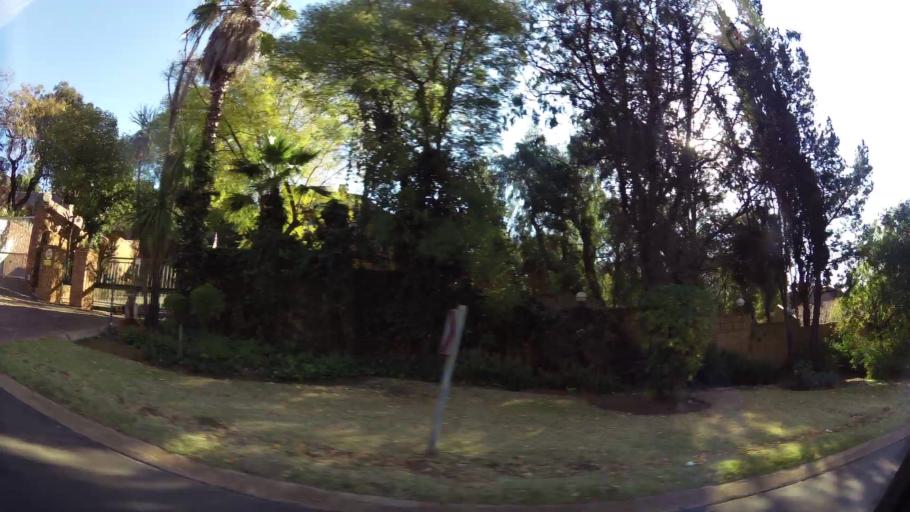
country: ZA
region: Gauteng
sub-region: City of Johannesburg Metropolitan Municipality
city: Johannesburg
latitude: -26.2892
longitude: 28.0628
